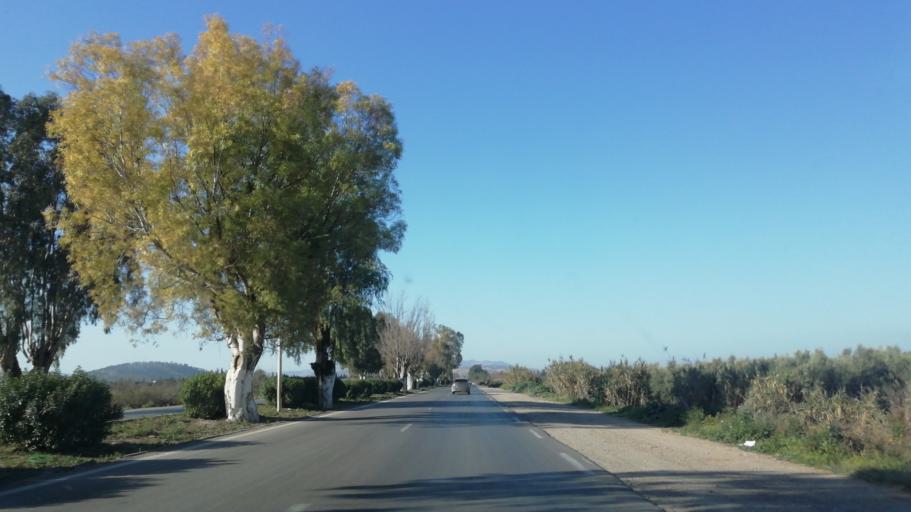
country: DZ
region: Mascara
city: Mascara
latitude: 35.6076
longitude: 0.0938
